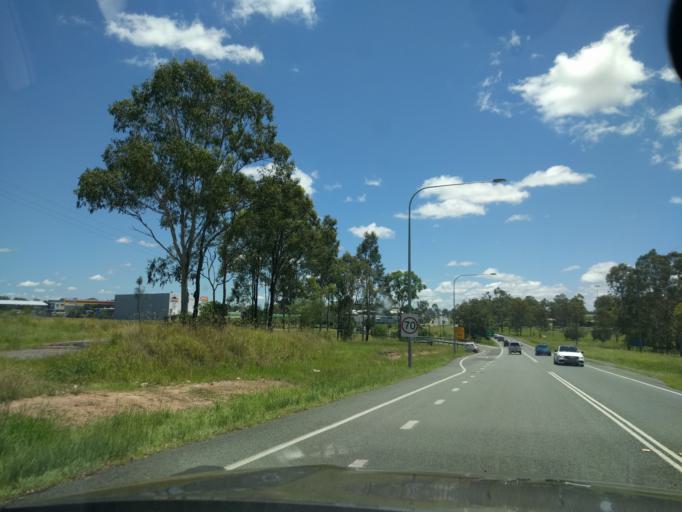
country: AU
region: Queensland
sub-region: Logan
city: Cedar Vale
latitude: -27.8385
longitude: 153.0254
